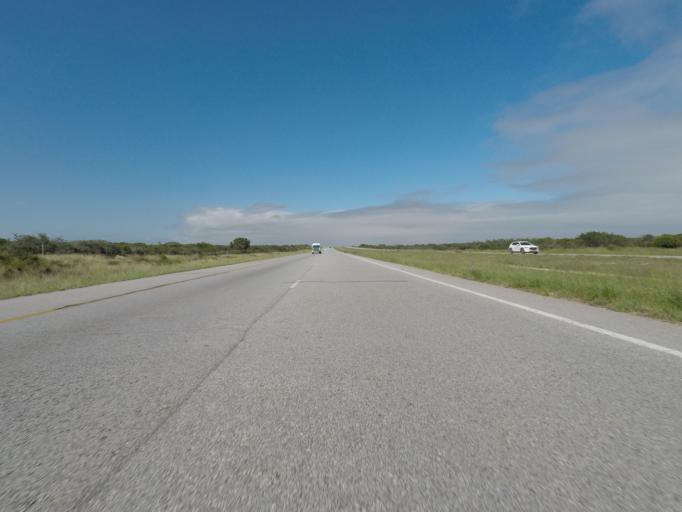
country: ZA
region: Eastern Cape
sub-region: Nelson Mandela Bay Metropolitan Municipality
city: Port Elizabeth
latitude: -33.7476
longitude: 25.7190
